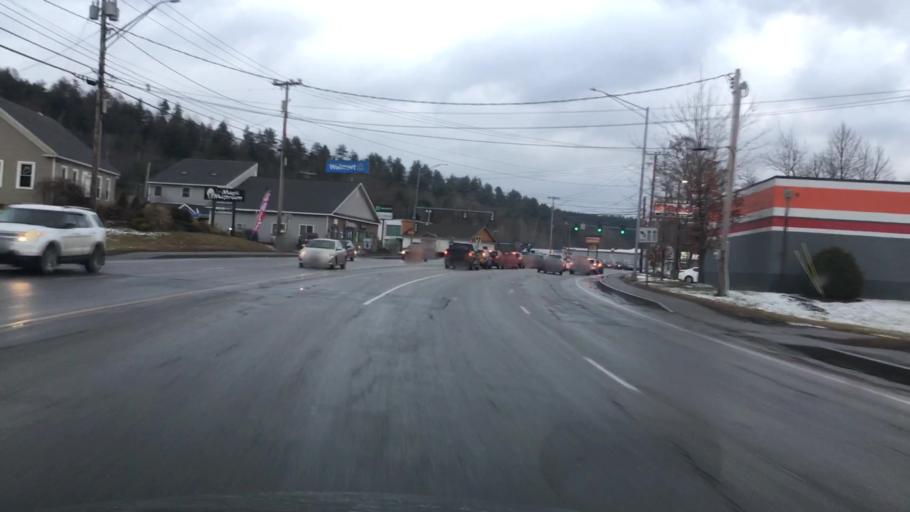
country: US
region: New Hampshire
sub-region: Sullivan County
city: Claremont
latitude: 43.3756
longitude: -72.3310
